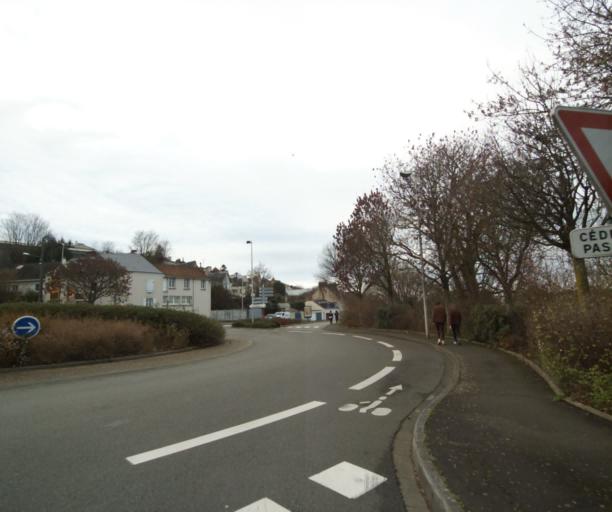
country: FR
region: Pays de la Loire
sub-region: Departement de la Sarthe
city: Coulaines
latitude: 48.0158
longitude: 0.2022
